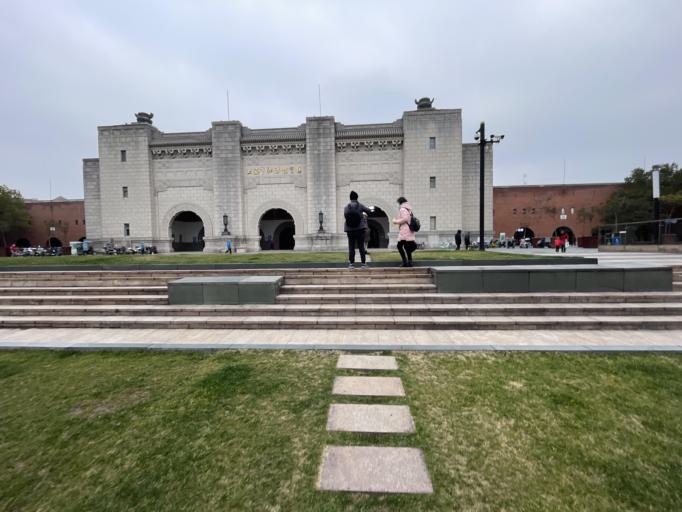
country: CN
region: Shanghai Shi
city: Yangpu
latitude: 31.3078
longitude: 121.5099
